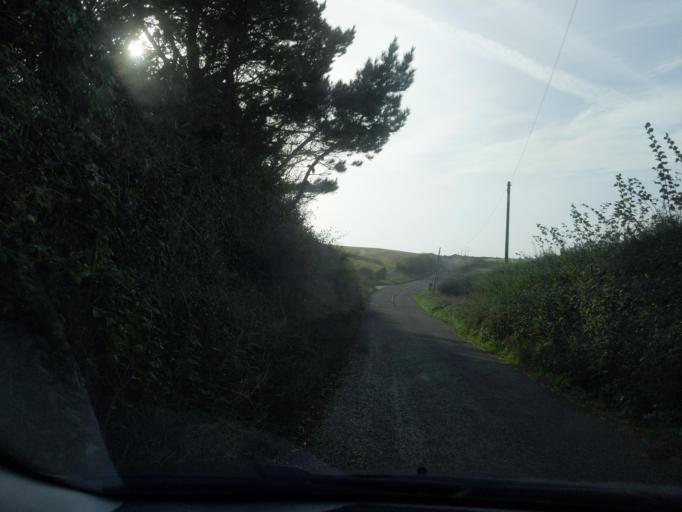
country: GB
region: England
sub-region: Cornwall
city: Pillaton
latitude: 50.3649
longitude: -4.3093
